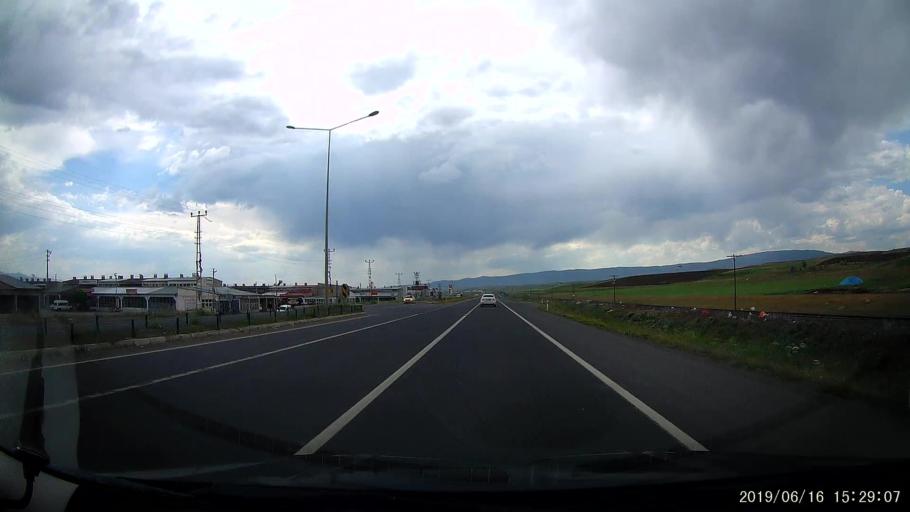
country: TR
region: Erzurum
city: Horasan
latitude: 40.0313
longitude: 42.1393
